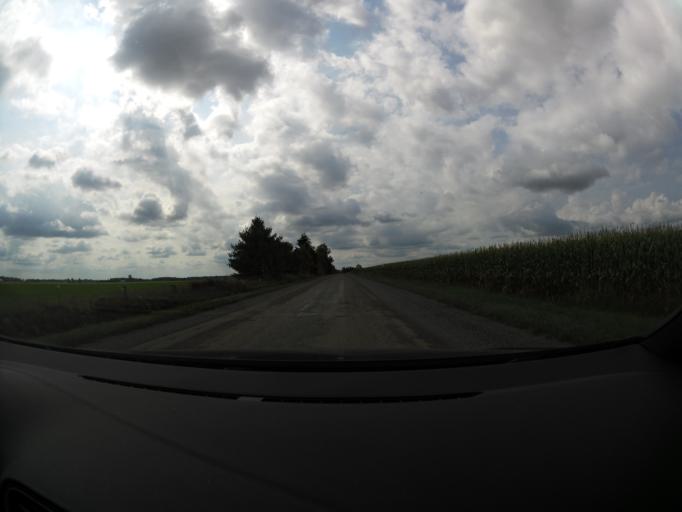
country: CA
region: Ontario
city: Arnprior
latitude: 45.3929
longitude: -76.2466
